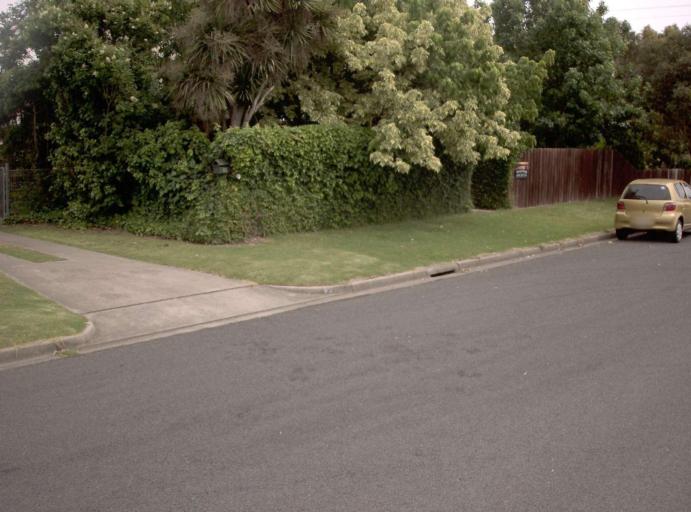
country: AU
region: Victoria
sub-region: Wellington
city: Sale
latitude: -37.9631
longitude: 147.0806
